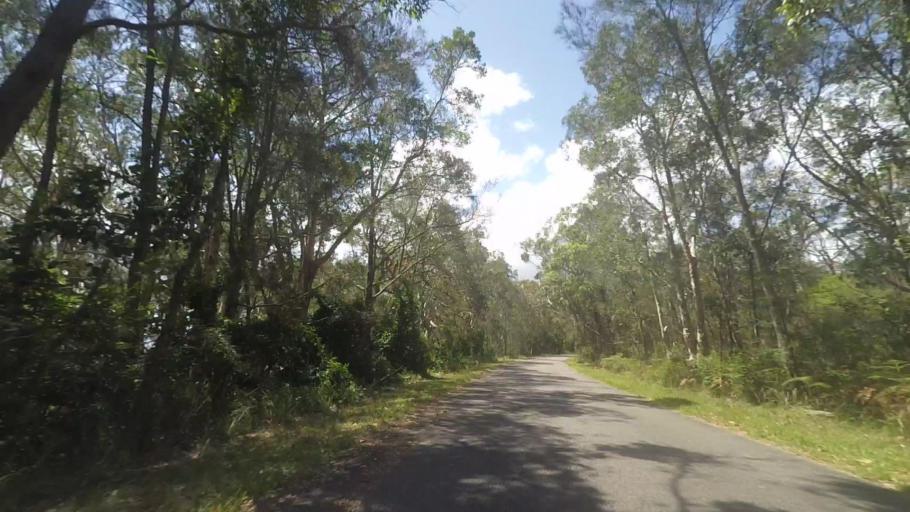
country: AU
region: New South Wales
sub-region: Great Lakes
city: Bulahdelah
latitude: -32.5187
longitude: 152.3221
